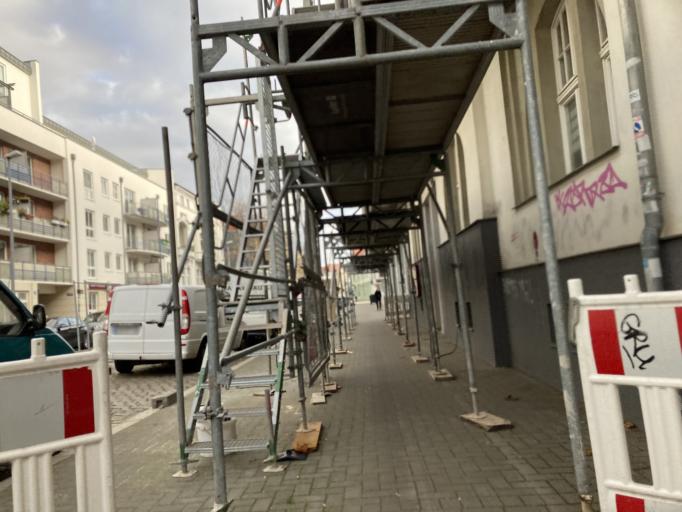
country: DE
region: Saxony-Anhalt
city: Magdeburg
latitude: 52.1314
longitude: 11.6167
